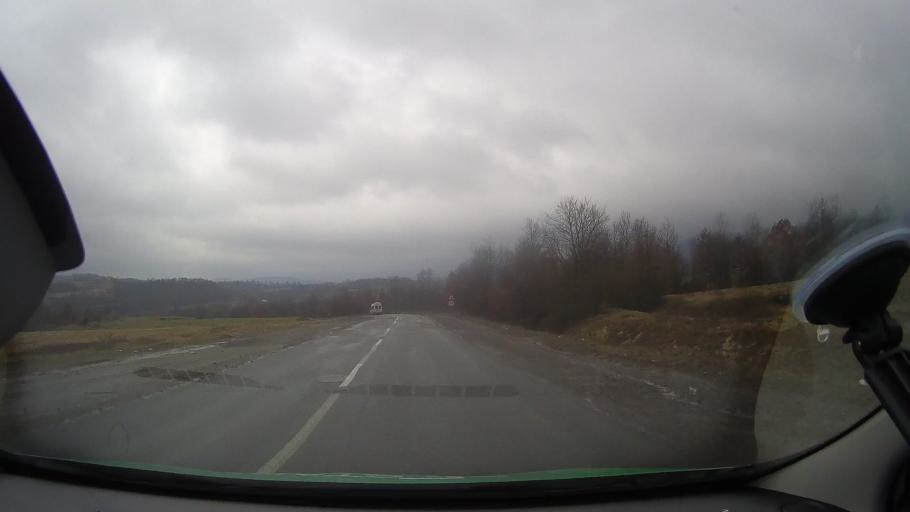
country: RO
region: Arad
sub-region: Comuna Varfurile
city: Varfurile
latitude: 46.2936
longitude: 22.5414
